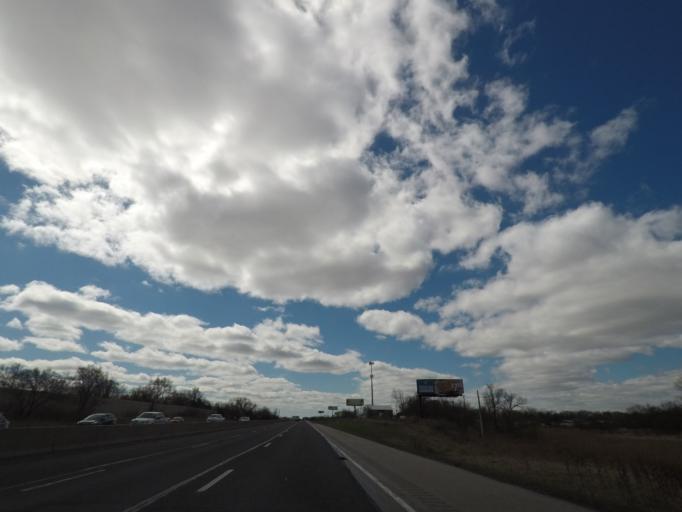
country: US
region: Illinois
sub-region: Will County
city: Plainfield
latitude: 41.6287
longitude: -88.1637
